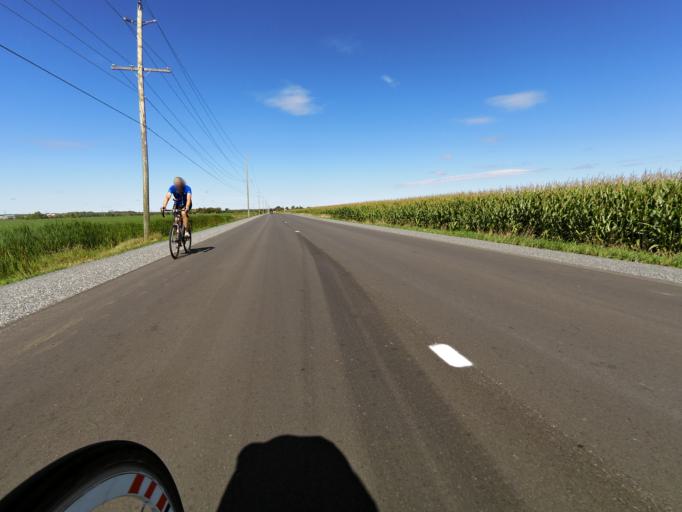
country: CA
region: Ontario
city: Bells Corners
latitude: 45.2312
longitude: -75.8656
